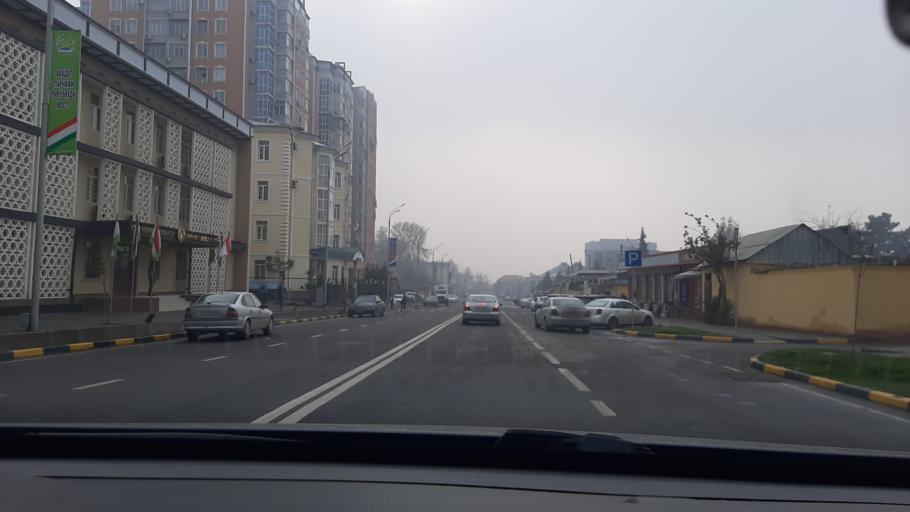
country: TJ
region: Dushanbe
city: Dushanbe
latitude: 38.5616
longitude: 68.7948
